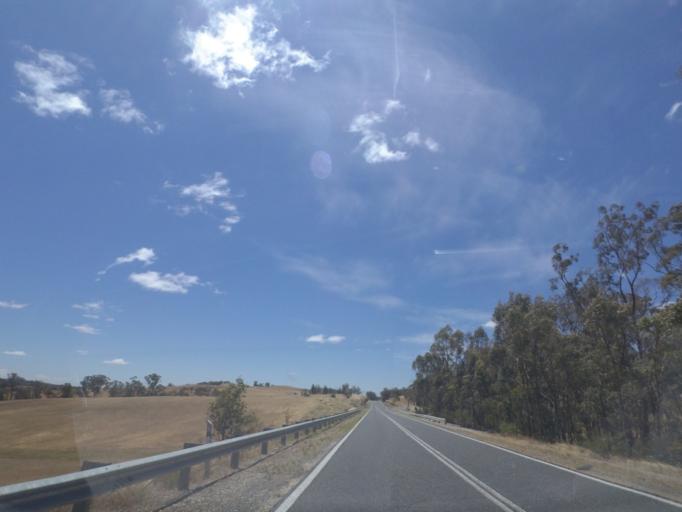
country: AU
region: Victoria
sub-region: Mount Alexander
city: Castlemaine
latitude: -37.2125
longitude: 144.1401
